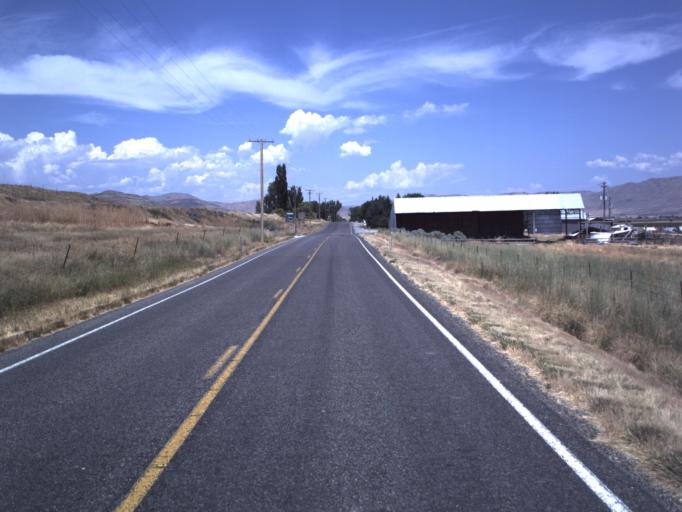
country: US
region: Utah
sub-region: Box Elder County
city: Tremonton
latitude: 41.6630
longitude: -112.2964
